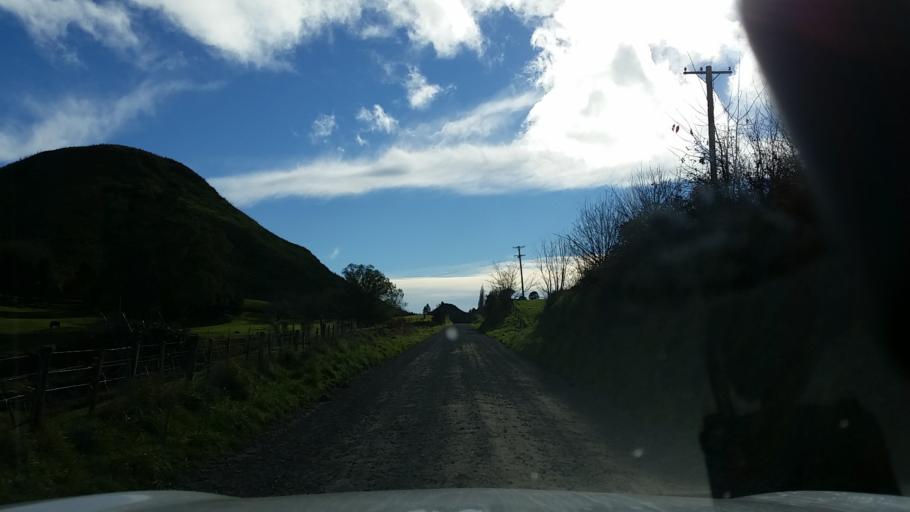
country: NZ
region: Bay of Plenty
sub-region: Rotorua District
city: Rotorua
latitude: -38.3670
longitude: 176.2075
